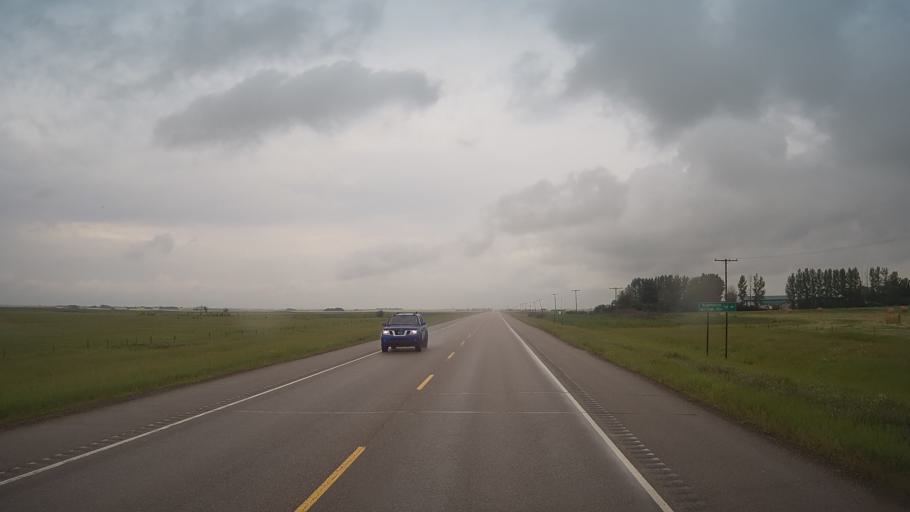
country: CA
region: Saskatchewan
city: Unity
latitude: 52.4349
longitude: -108.9729
